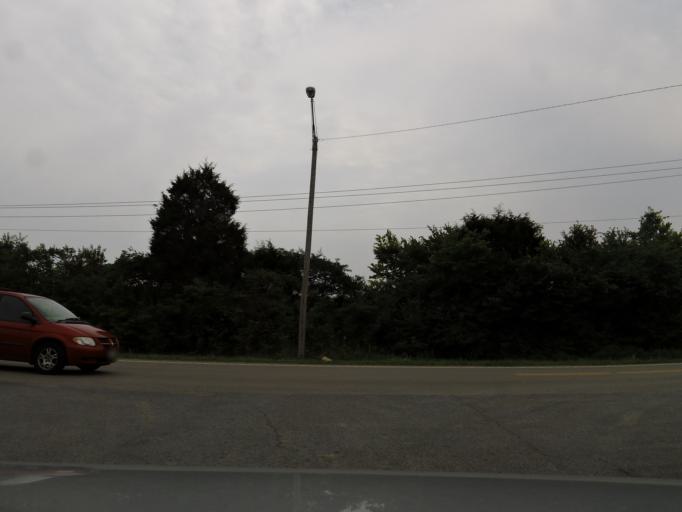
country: US
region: Ohio
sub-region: Warren County
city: Waynesville
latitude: 39.5209
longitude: -84.0629
